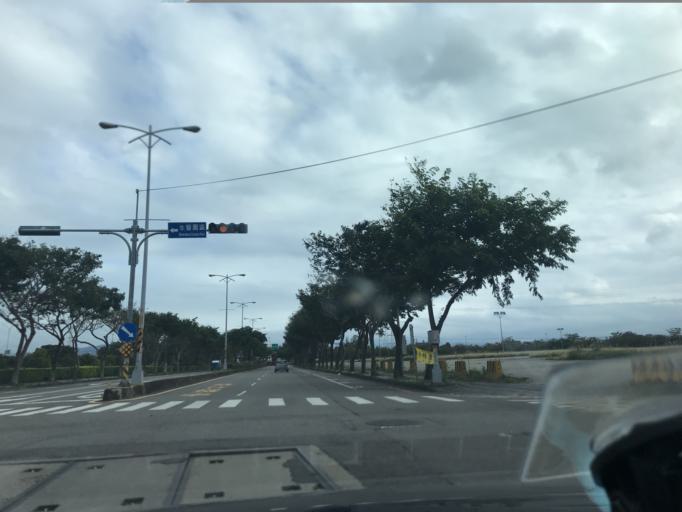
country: TW
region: Taiwan
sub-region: Hsinchu
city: Zhubei
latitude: 24.8044
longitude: 121.0436
